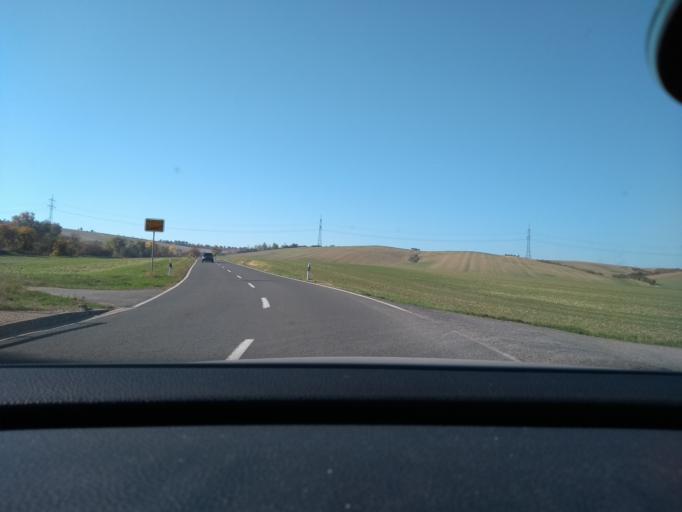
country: DE
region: Saxony-Anhalt
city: Erdeborn
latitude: 51.4676
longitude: 11.6277
